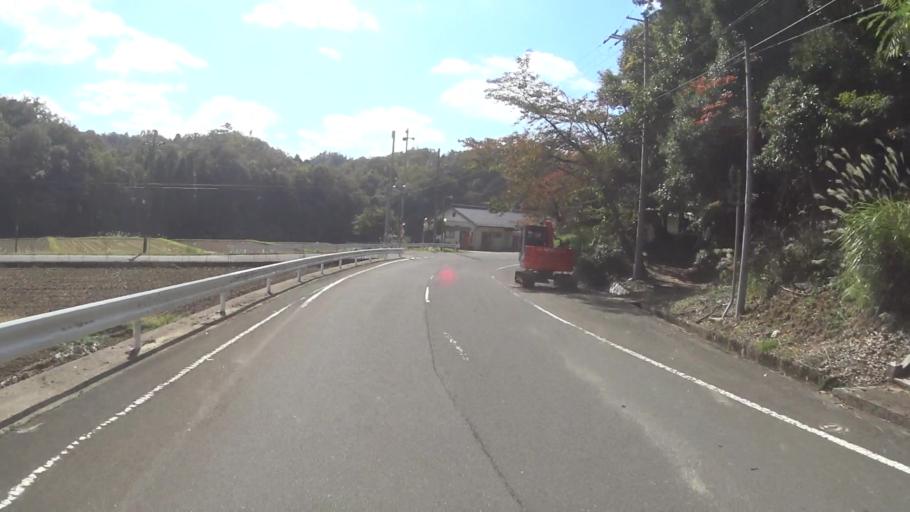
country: JP
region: Hyogo
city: Toyooka
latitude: 35.5993
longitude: 134.9833
